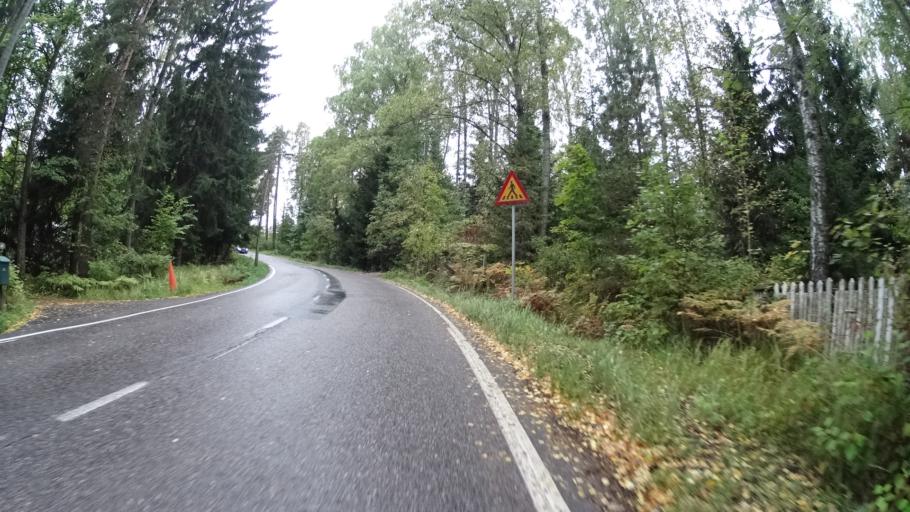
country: FI
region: Uusimaa
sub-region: Helsinki
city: Kauniainen
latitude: 60.2536
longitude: 24.7282
